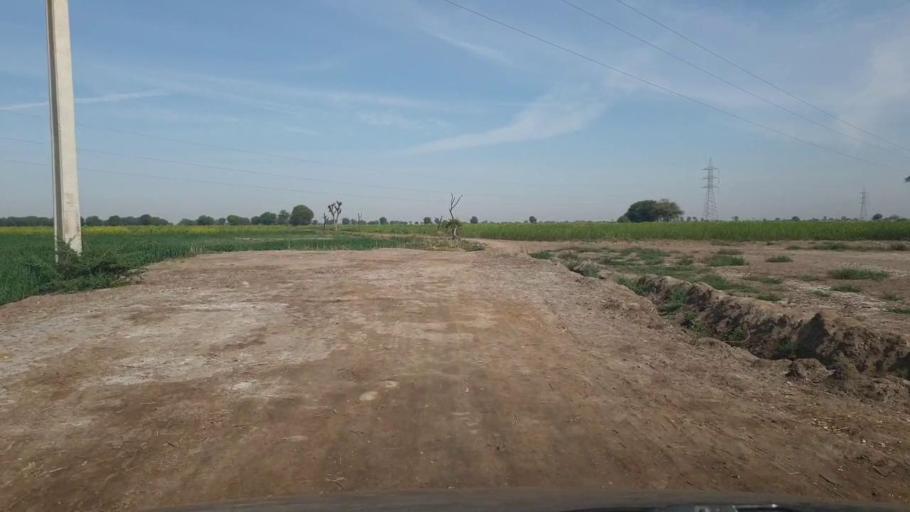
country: PK
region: Sindh
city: Umarkot
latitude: 25.3649
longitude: 69.6089
